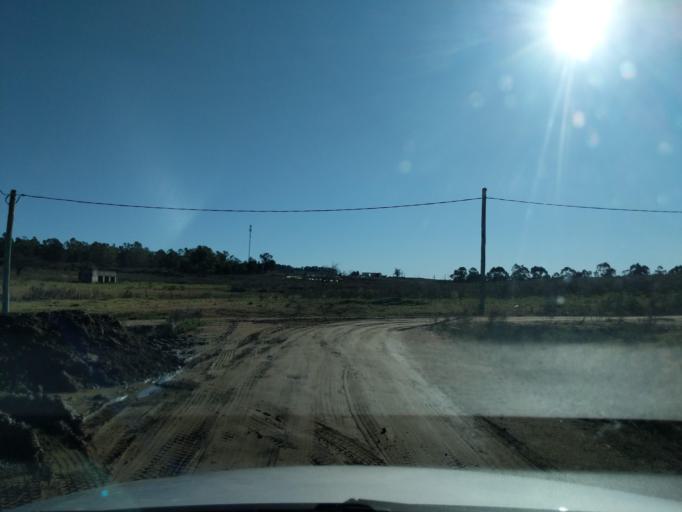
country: UY
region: Florida
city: Florida
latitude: -34.0803
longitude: -56.2401
